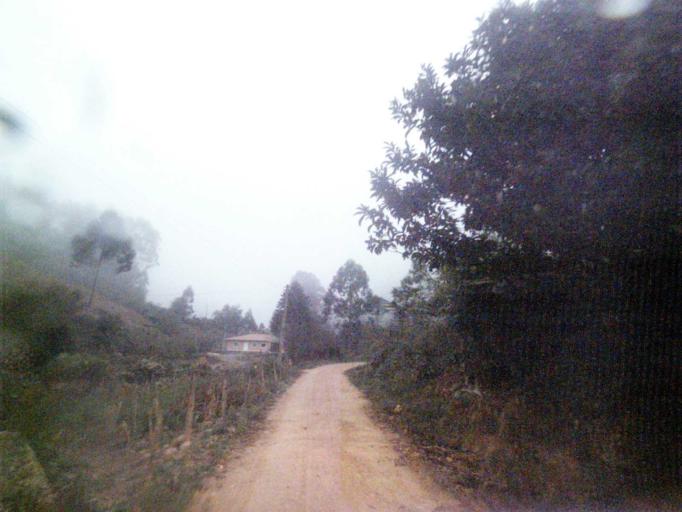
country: BR
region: Santa Catarina
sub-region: Anitapolis
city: Anitapolis
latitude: -27.7960
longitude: -49.1388
